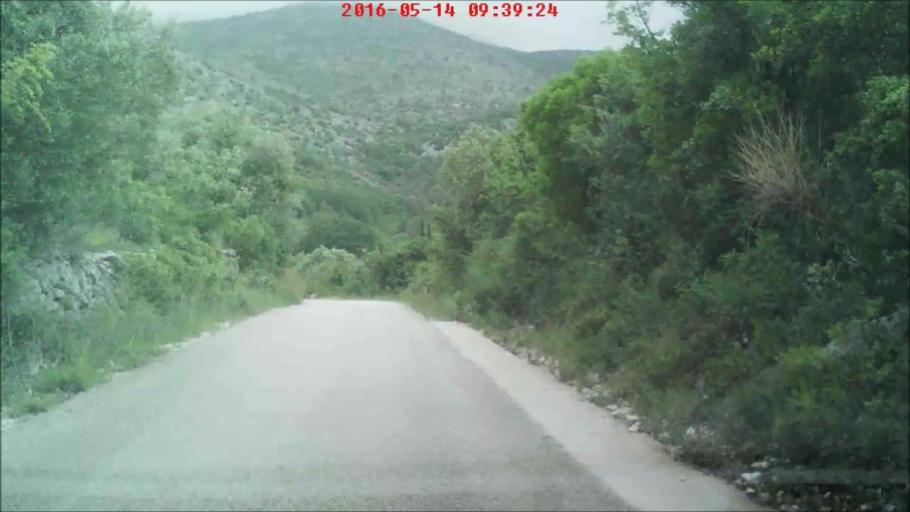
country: HR
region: Dubrovacko-Neretvanska
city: Podgora
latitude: 42.7903
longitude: 17.8910
